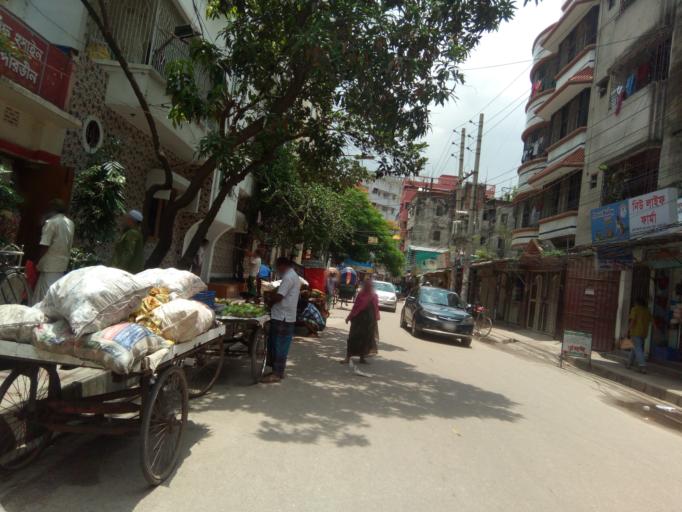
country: BD
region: Dhaka
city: Azimpur
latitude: 23.7674
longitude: 90.3626
